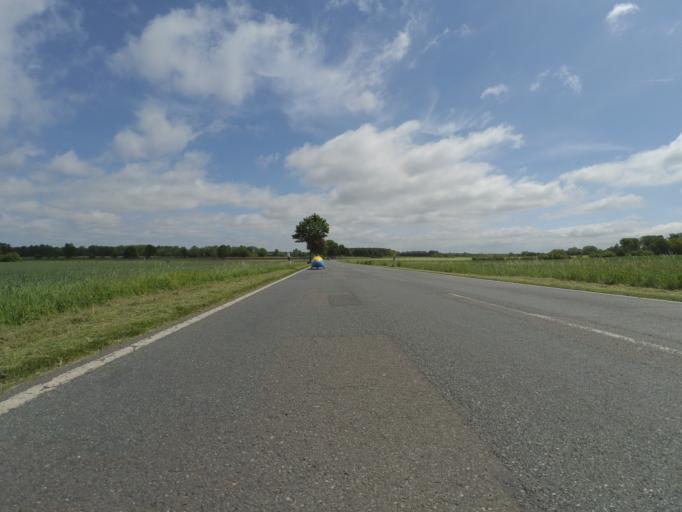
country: DE
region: Lower Saxony
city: Leiferde
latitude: 52.4388
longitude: 10.4489
